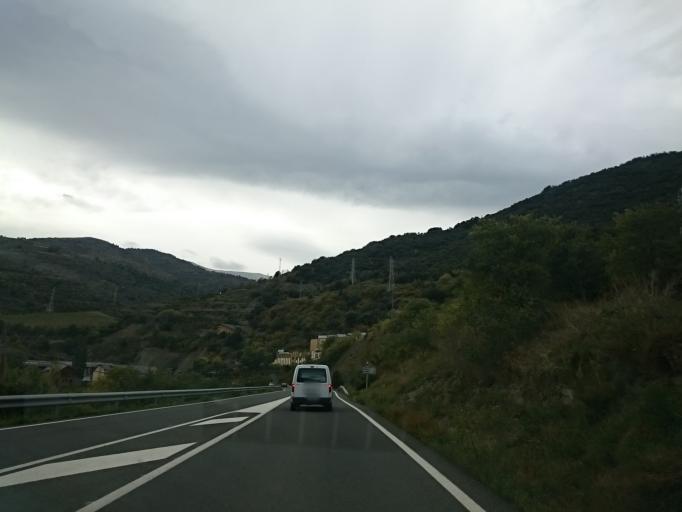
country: ES
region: Catalonia
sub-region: Provincia de Lleida
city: Sort
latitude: 42.4478
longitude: 1.1397
